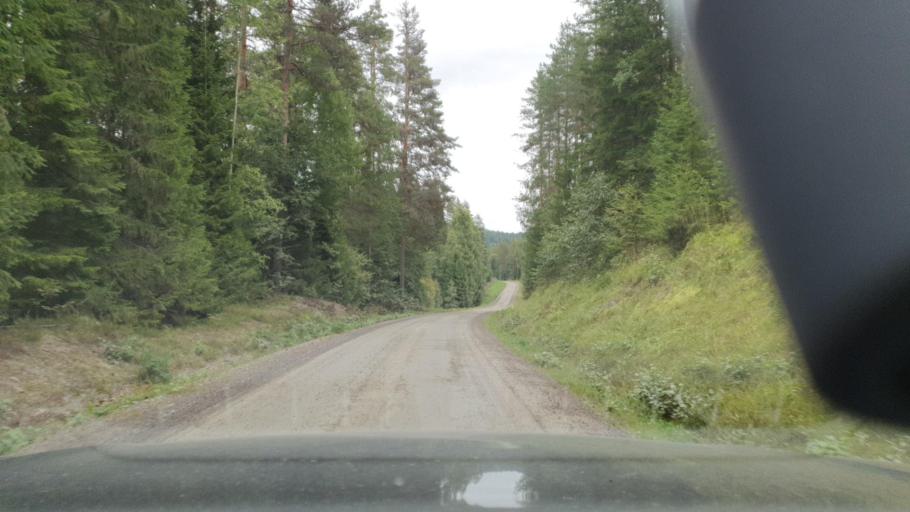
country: SE
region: Vaermland
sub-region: Torsby Kommun
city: Torsby
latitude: 60.3849
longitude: 12.8928
